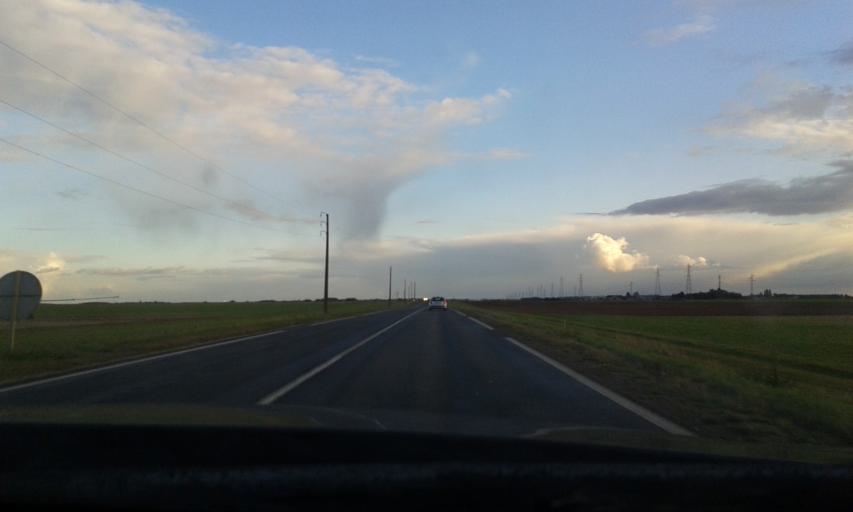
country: FR
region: Centre
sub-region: Departement d'Eure-et-Loir
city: Voves
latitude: 48.3126
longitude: 1.6809
